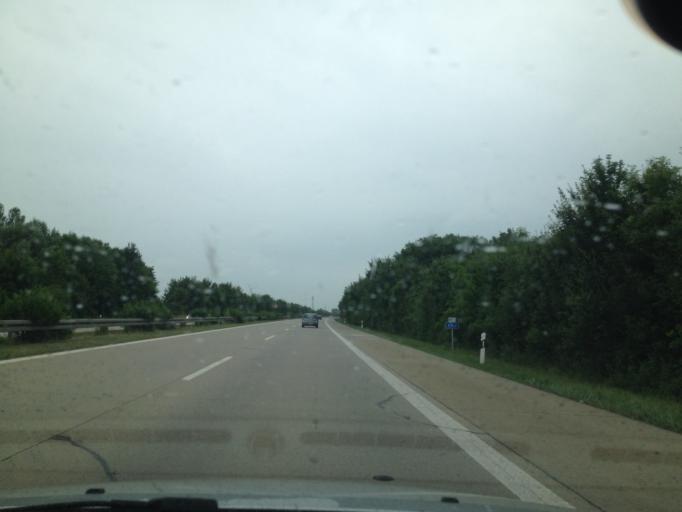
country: DE
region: Bavaria
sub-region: Regierungsbezirk Unterfranken
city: Sulzfeld am Main
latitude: 49.7241
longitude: 10.1028
